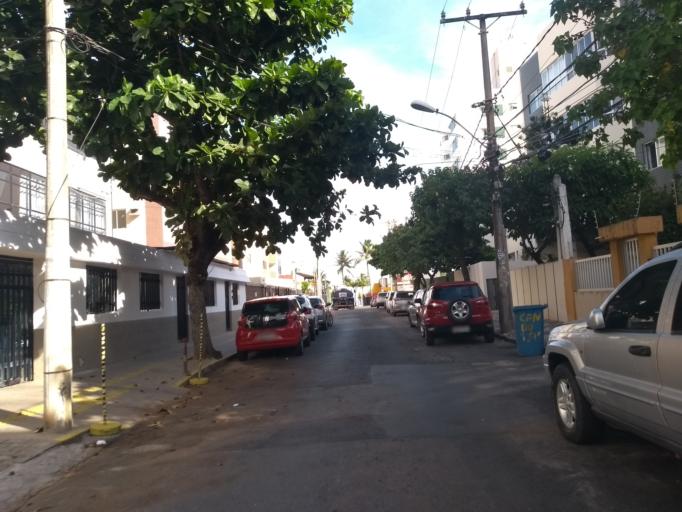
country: BR
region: Bahia
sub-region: Salvador
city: Salvador
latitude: -12.9968
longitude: -38.4486
